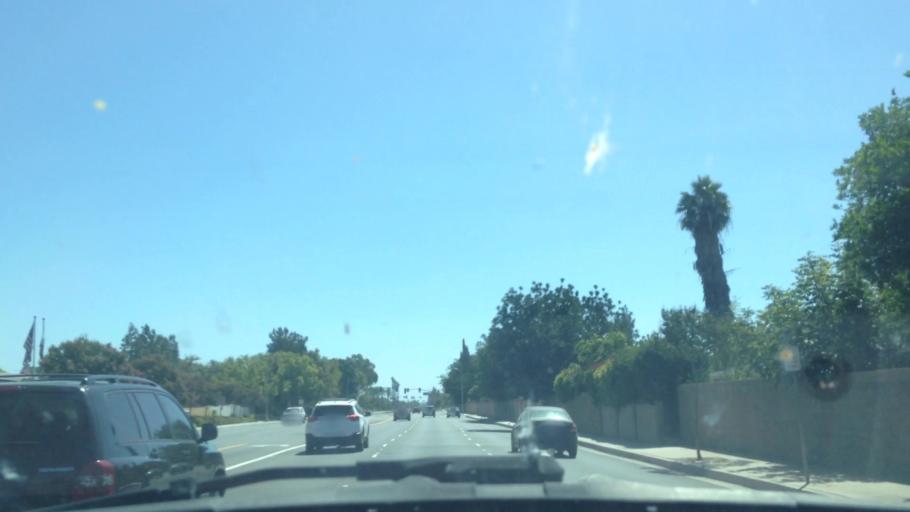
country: US
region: California
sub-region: Orange County
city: Placentia
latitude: 33.8841
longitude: -117.8898
